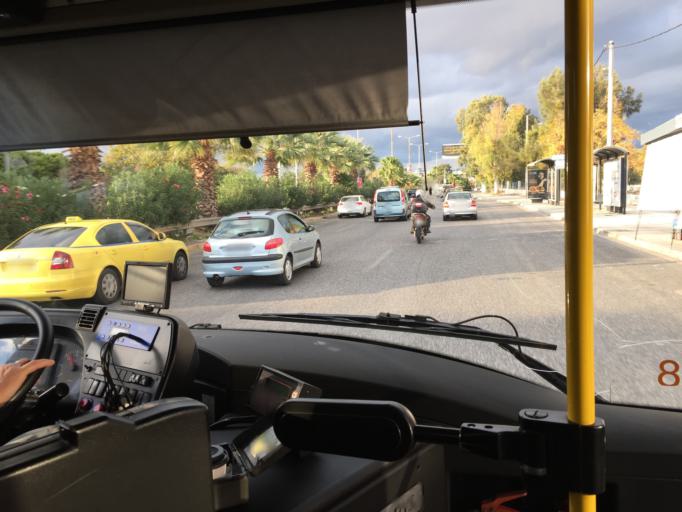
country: GR
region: Attica
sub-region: Nomarchia Athinas
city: Alimos
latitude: 37.8986
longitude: 23.7203
